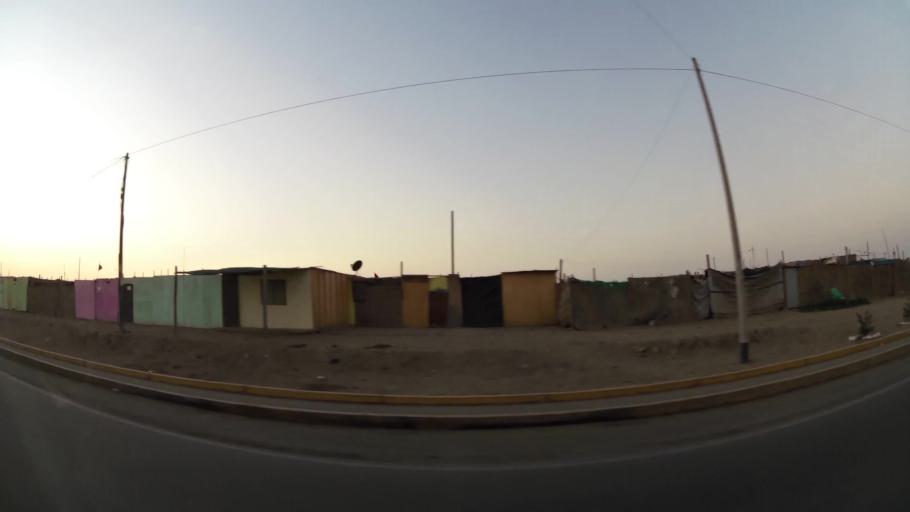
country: PE
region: Ica
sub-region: Provincia de Pisco
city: Pisco
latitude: -13.7113
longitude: -76.1872
